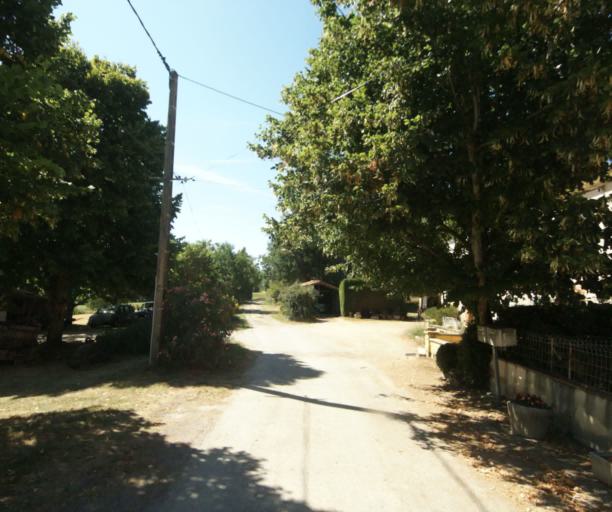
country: FR
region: Midi-Pyrenees
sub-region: Departement de la Haute-Garonne
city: Saint-Felix-Lauragais
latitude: 43.4970
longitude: 1.9375
